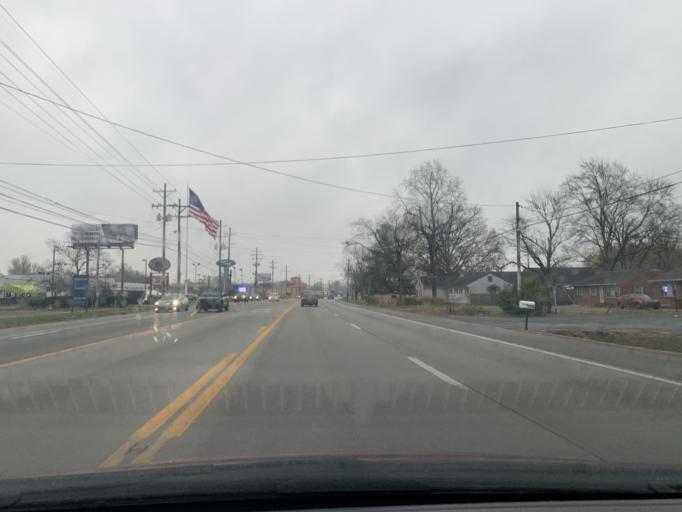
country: US
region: Kentucky
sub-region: Jefferson County
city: Okolona
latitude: 38.1646
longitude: -85.7023
